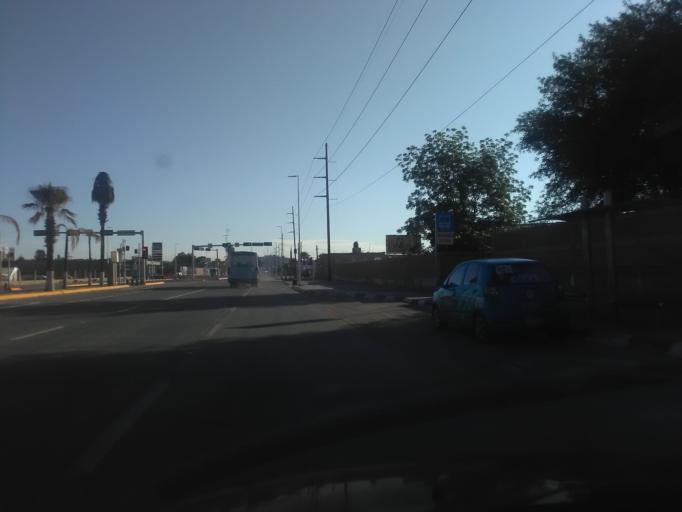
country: MX
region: Durango
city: Victoria de Durango
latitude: 23.9982
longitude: -104.7012
